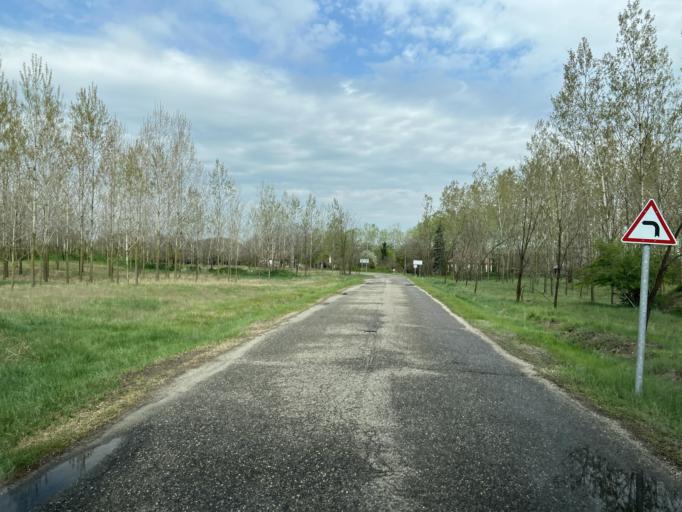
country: HU
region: Pest
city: Hernad
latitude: 47.1764
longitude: 19.4767
